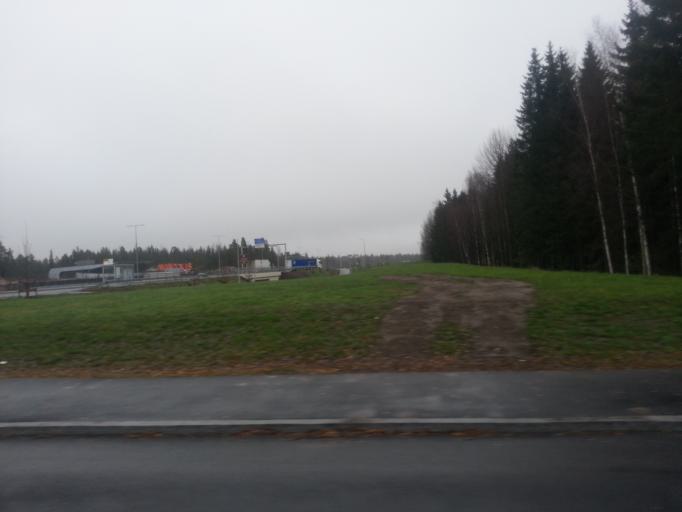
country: FI
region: Uusimaa
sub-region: Helsinki
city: Vantaa
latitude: 60.3018
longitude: 24.9514
